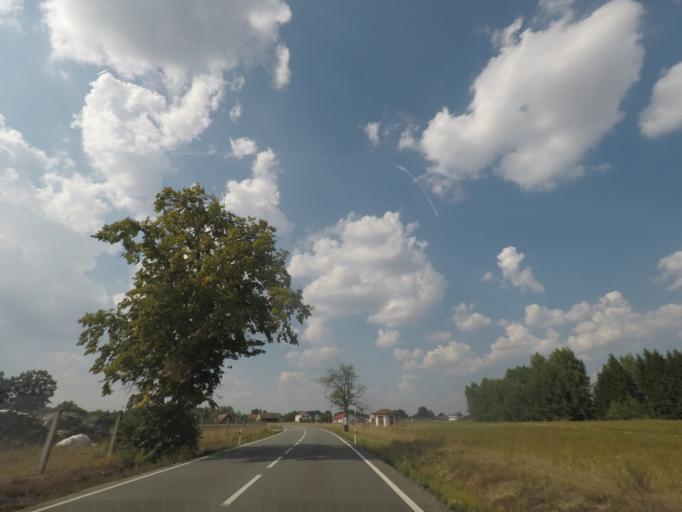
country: CZ
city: Borohradek
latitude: 50.1144
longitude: 16.0729
